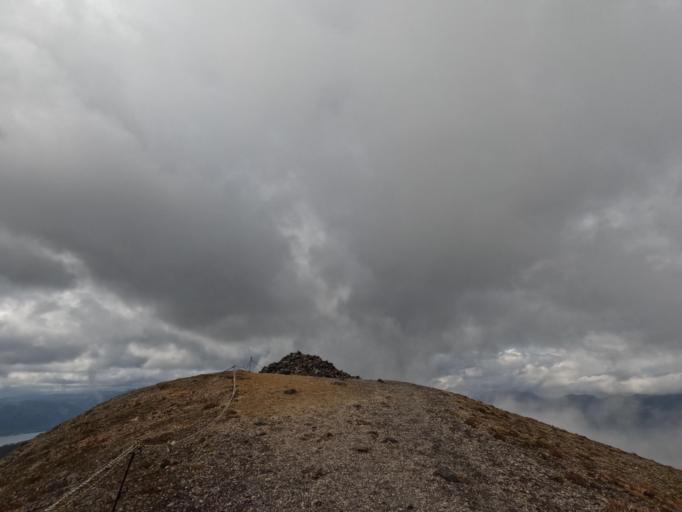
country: JP
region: Hokkaido
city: Shiraoi
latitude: 42.6921
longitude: 141.3865
